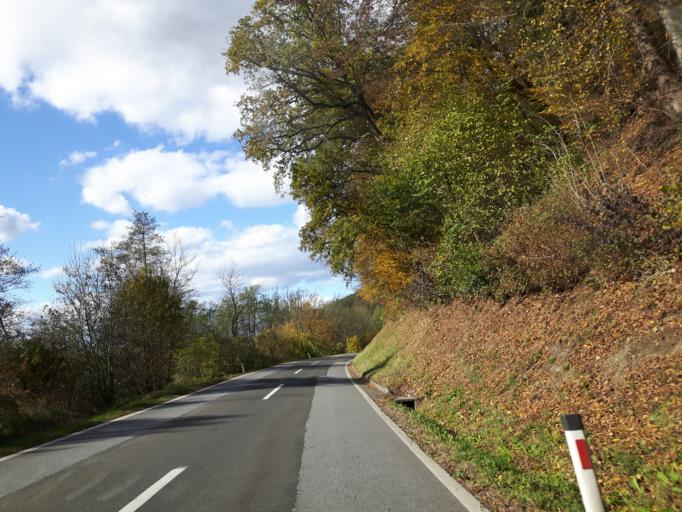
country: AT
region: Styria
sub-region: Politischer Bezirk Leibnitz
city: Kitzeck im Sausal
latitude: 46.7592
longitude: 15.4152
